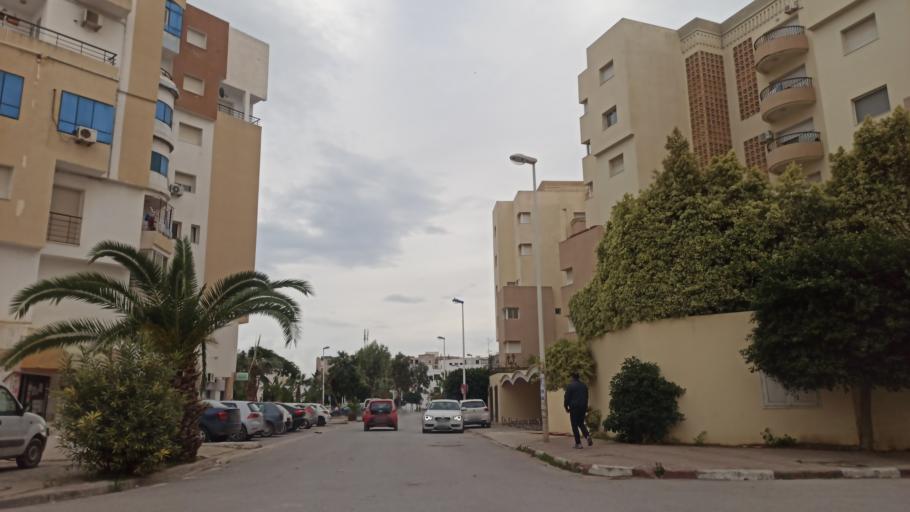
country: TN
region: Tunis
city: La Goulette
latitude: 36.8596
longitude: 10.2649
